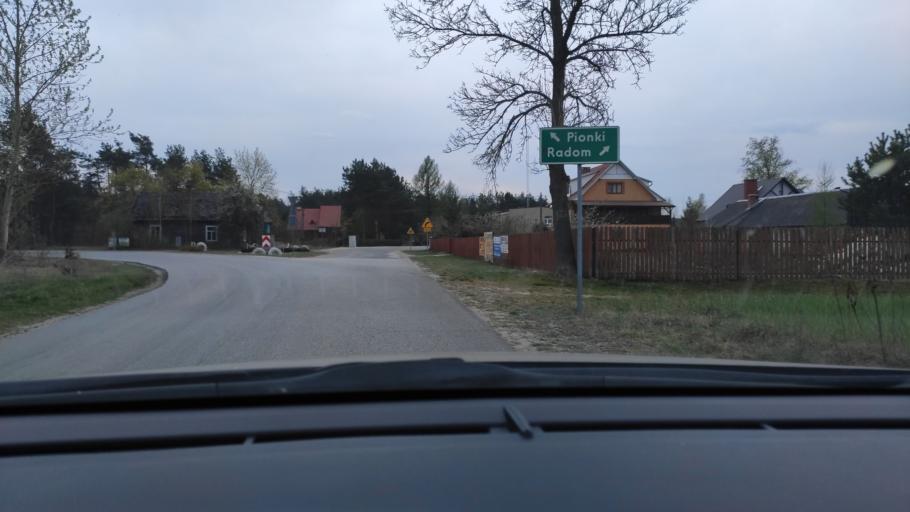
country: PL
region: Masovian Voivodeship
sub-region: Powiat radomski
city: Pionki
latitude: 51.5505
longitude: 21.3679
